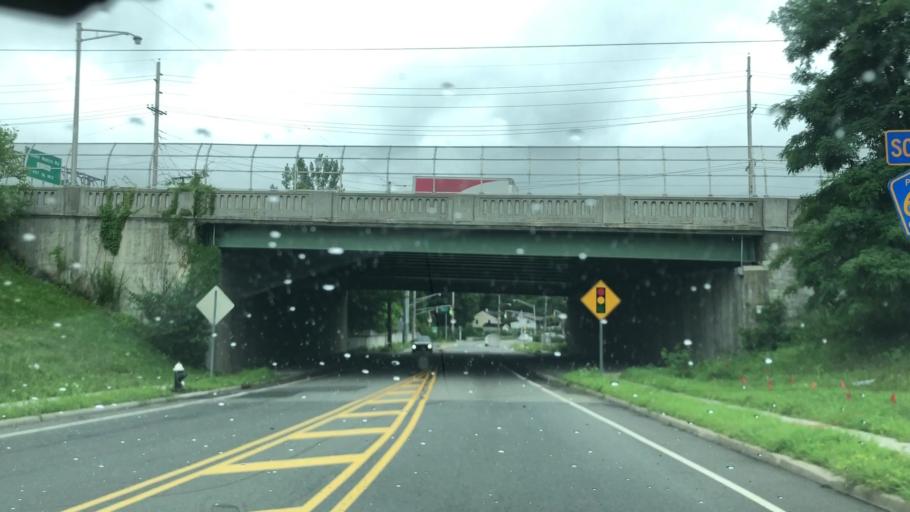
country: US
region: New Jersey
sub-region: Passaic County
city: Little Falls
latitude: 40.8827
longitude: -74.2095
